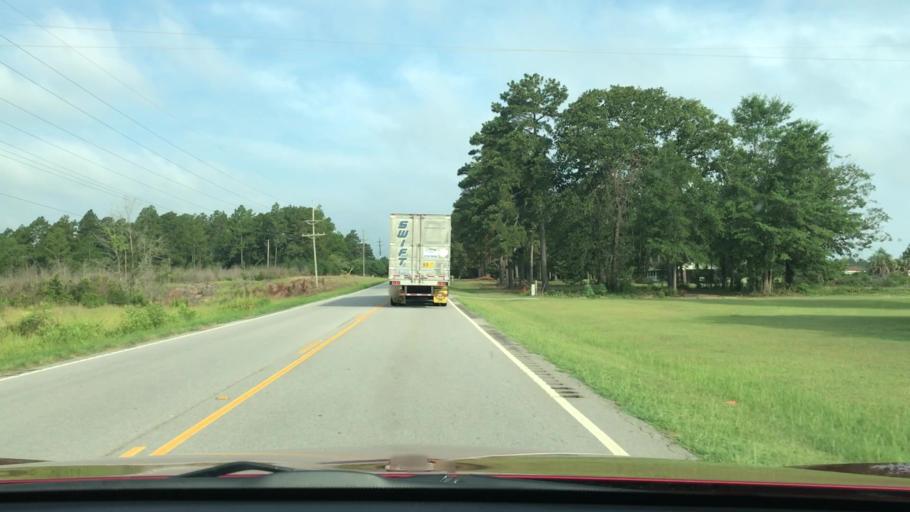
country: US
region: South Carolina
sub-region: Barnwell County
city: Williston
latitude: 33.6399
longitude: -81.3326
